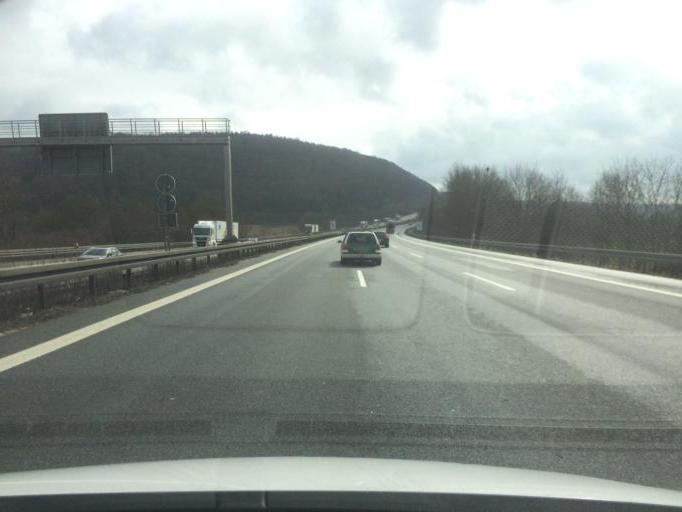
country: DE
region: Bavaria
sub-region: Regierungsbezirk Mittelfranken
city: Greding
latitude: 48.9951
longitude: 11.3784
